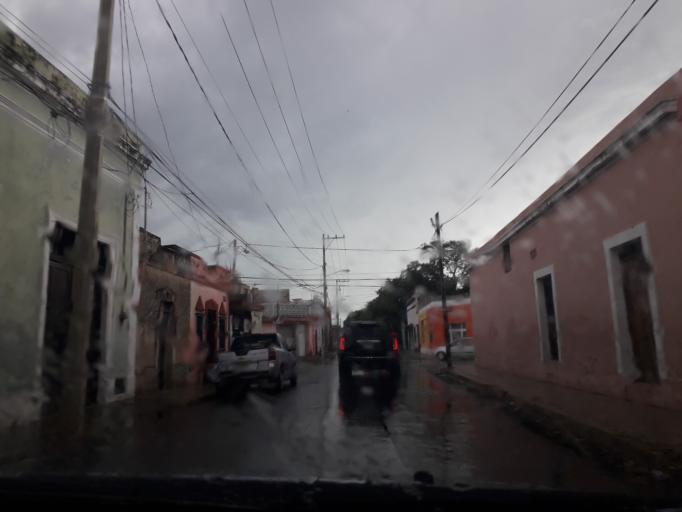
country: MX
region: Yucatan
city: Merida
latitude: 20.9689
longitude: -89.6322
